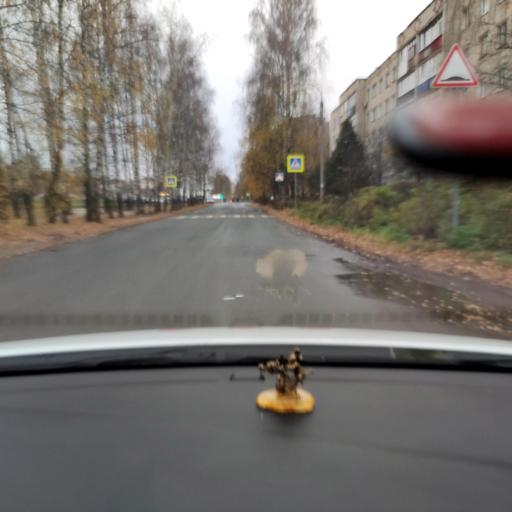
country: RU
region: Tatarstan
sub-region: Zelenodol'skiy Rayon
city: Zelenodolsk
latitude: 55.8508
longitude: 48.5644
